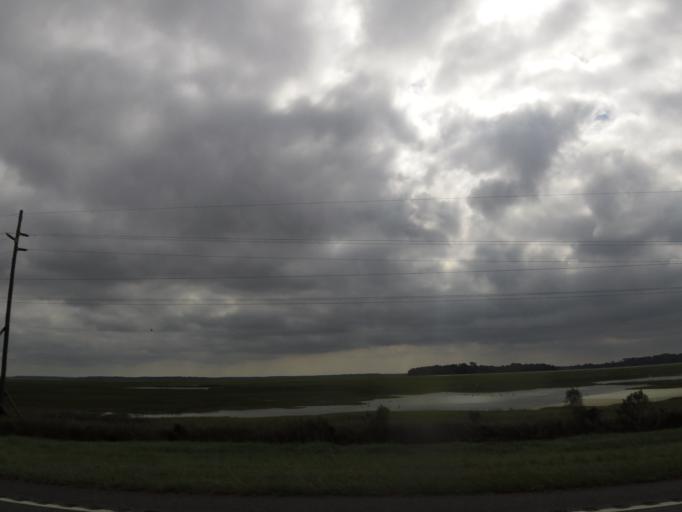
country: US
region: Georgia
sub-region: Glynn County
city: Brunswick
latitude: 31.0950
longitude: -81.4848
